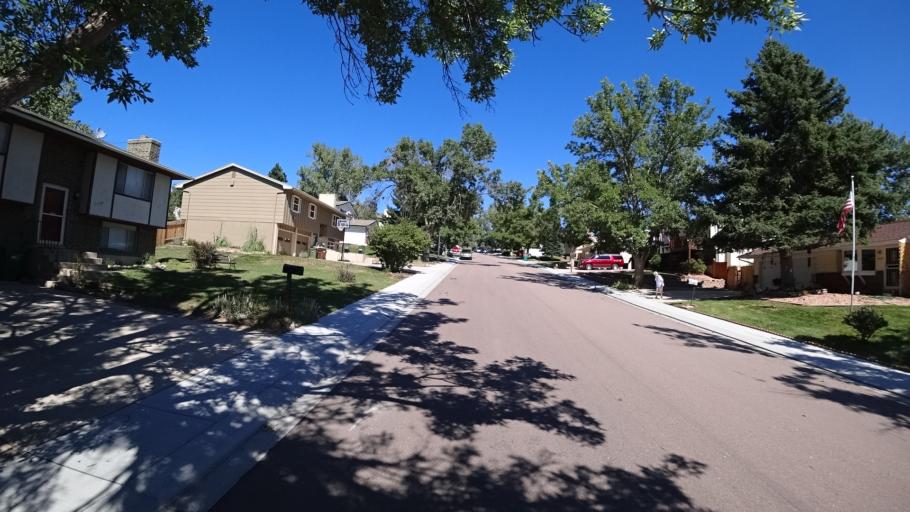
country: US
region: Colorado
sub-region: El Paso County
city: Cimarron Hills
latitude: 38.8785
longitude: -104.7336
